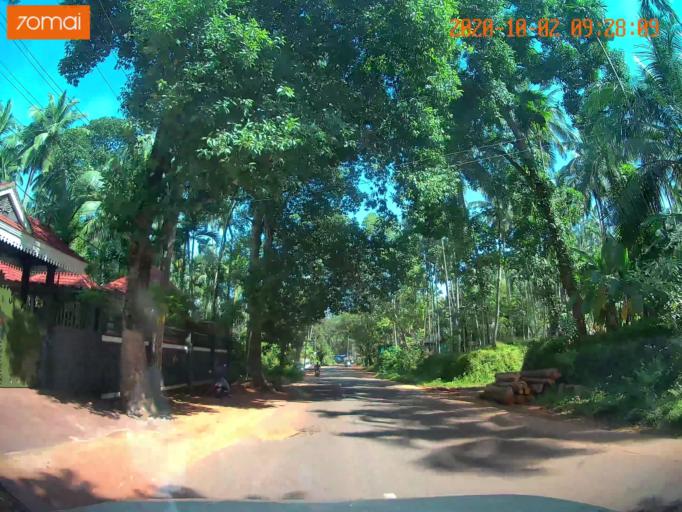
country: IN
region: Kerala
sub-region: Kozhikode
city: Naduvannur
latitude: 11.6044
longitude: 75.7637
